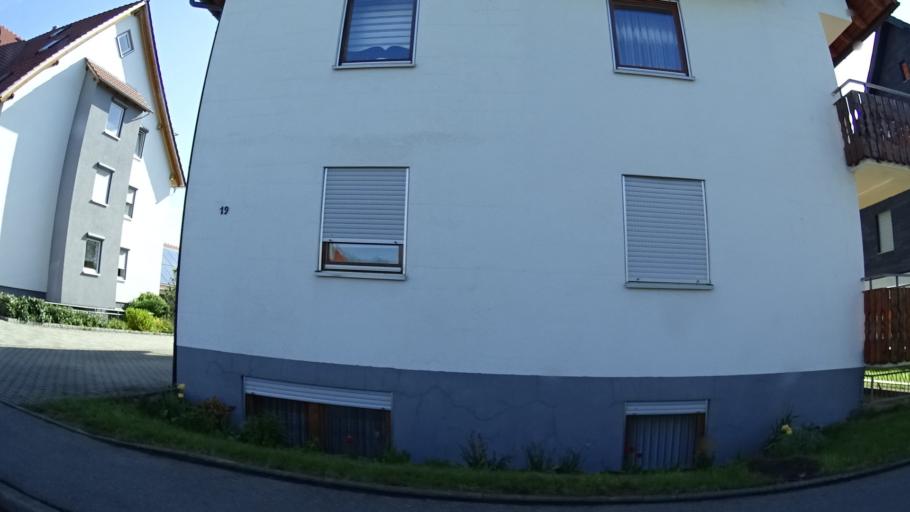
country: DE
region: Baden-Wuerttemberg
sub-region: Regierungsbezirk Stuttgart
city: Motzingen
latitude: 48.4929
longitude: 8.7547
